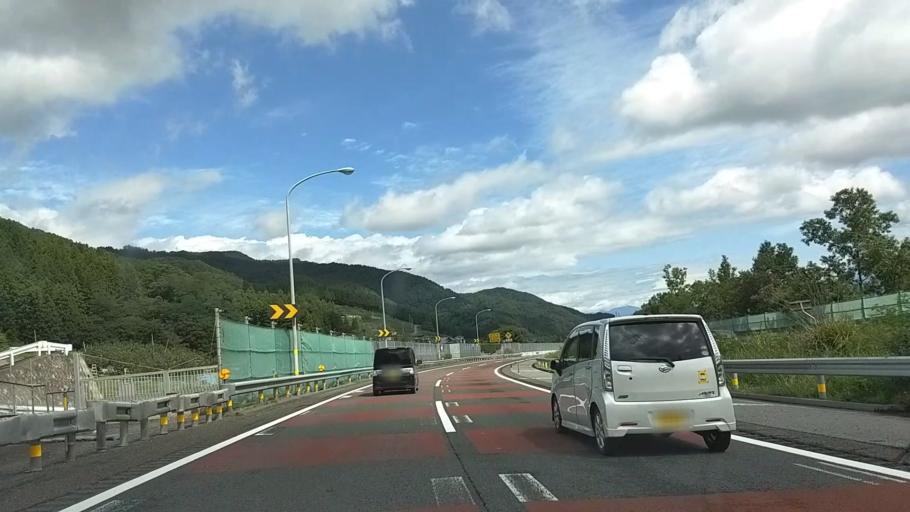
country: JP
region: Nagano
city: Nagano-shi
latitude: 36.5166
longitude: 138.0714
